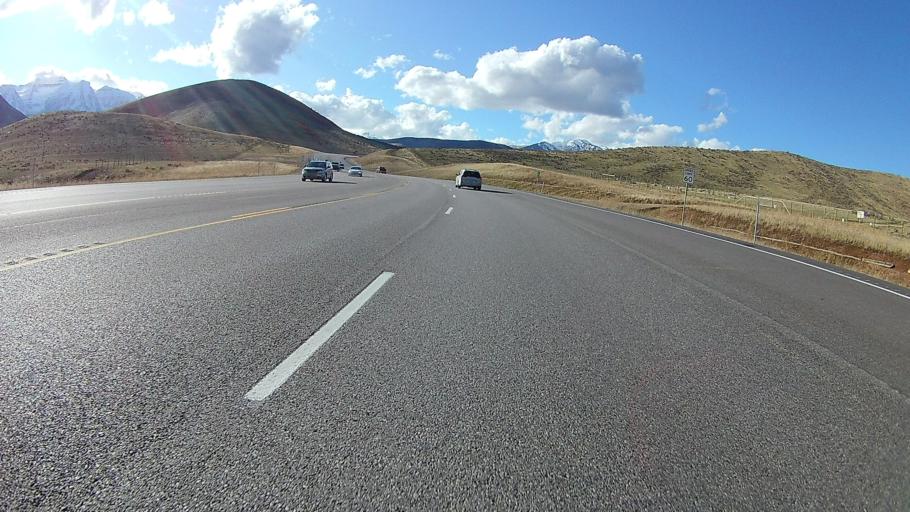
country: US
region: Utah
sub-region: Wasatch County
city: Midway
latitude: 40.4138
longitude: -111.4793
